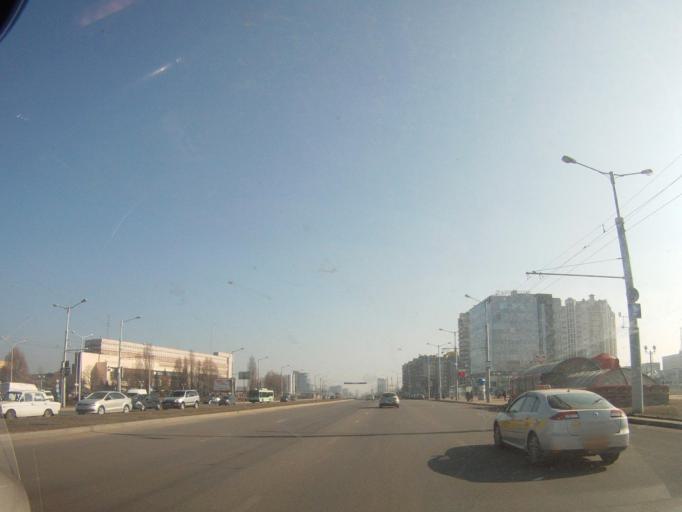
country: BY
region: Minsk
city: Novoye Medvezhino
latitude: 53.9061
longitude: 27.4544
